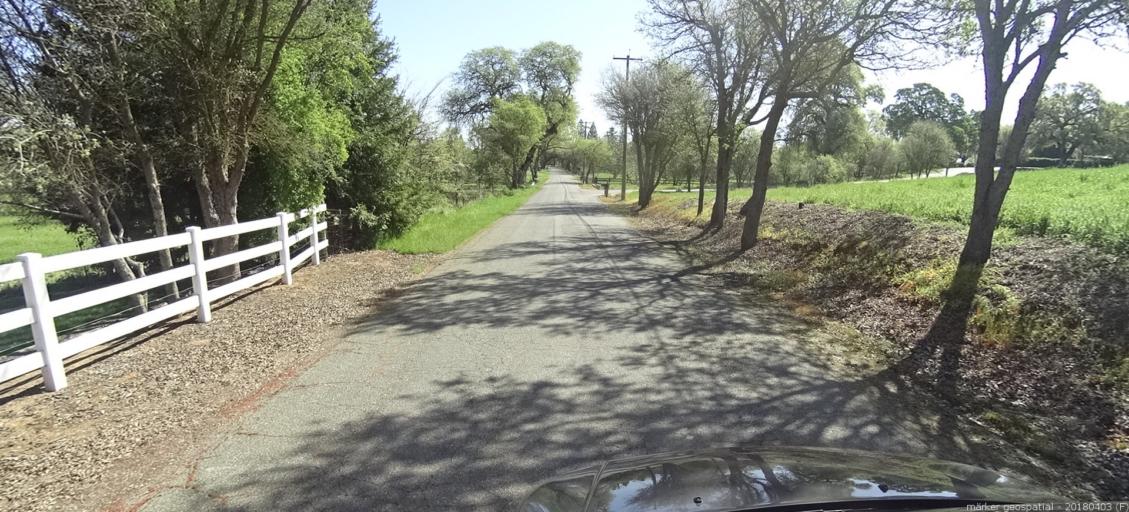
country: US
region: California
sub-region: Sacramento County
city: Wilton
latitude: 38.4209
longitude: -121.2081
